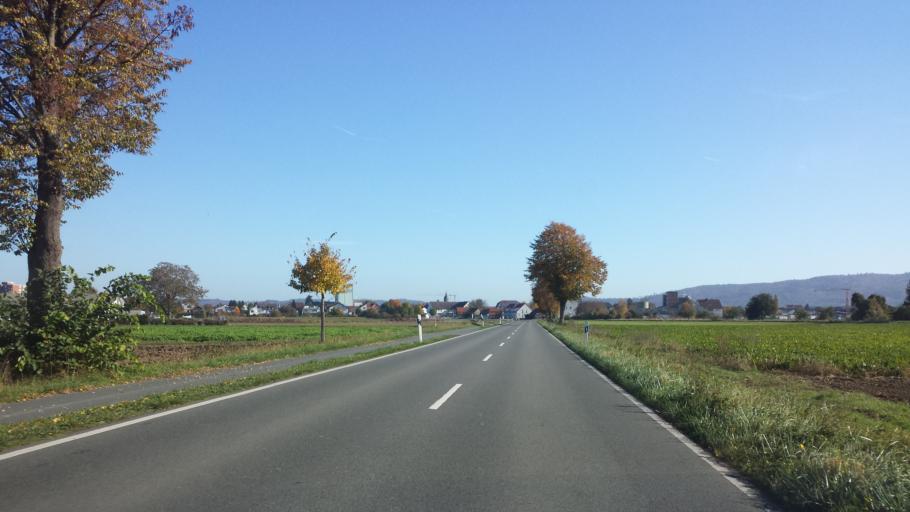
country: DE
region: Hesse
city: Pfungstadt
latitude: 49.7981
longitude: 8.5838
